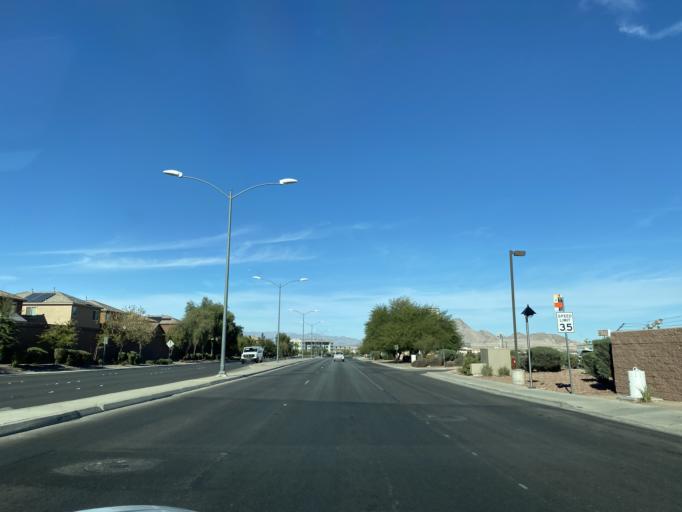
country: US
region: Nevada
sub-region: Clark County
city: Henderson
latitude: 36.0675
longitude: -115.0286
